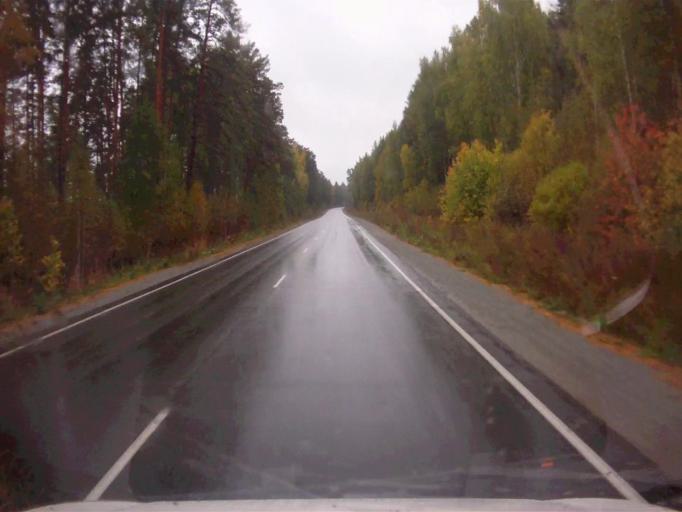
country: RU
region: Chelyabinsk
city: Kyshtym
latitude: 55.6385
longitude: 60.5933
